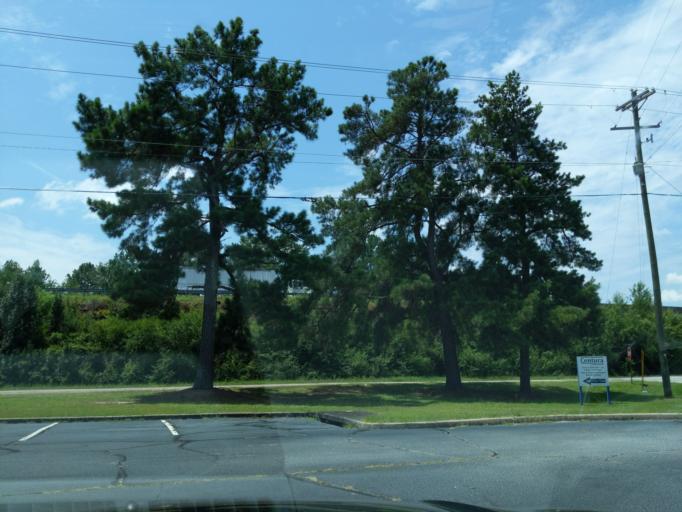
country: US
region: South Carolina
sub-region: Richland County
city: Dentsville
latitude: 34.0745
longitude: -80.9459
